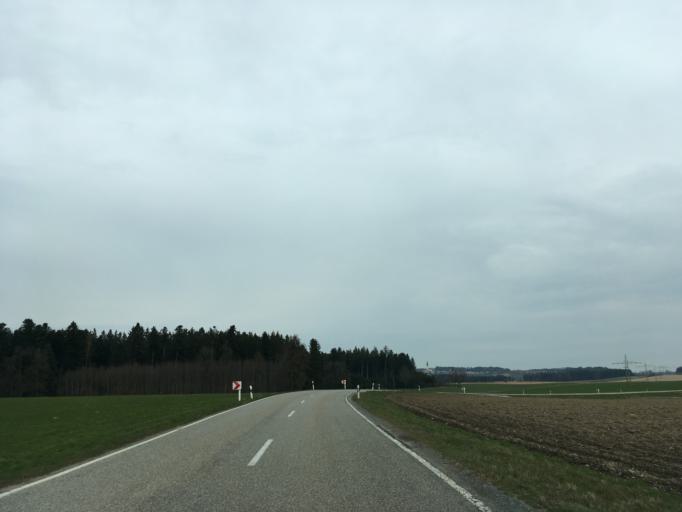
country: DE
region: Bavaria
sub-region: Upper Bavaria
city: Schnaitsee
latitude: 48.0415
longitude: 12.3704
